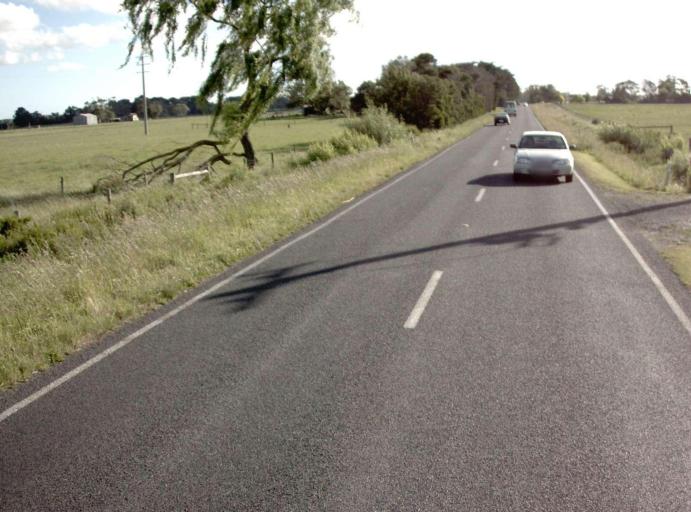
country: AU
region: Victoria
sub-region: Bass Coast
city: North Wonthaggi
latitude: -38.5179
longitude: 145.8965
